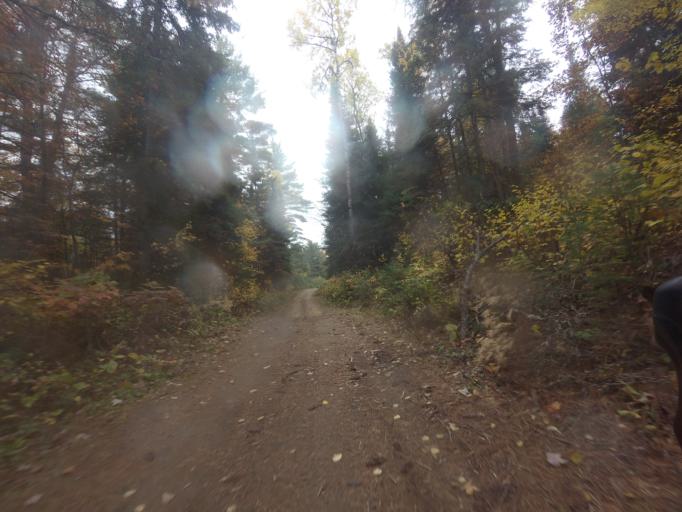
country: CA
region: Ontario
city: Petawawa
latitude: 45.7788
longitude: -77.3784
